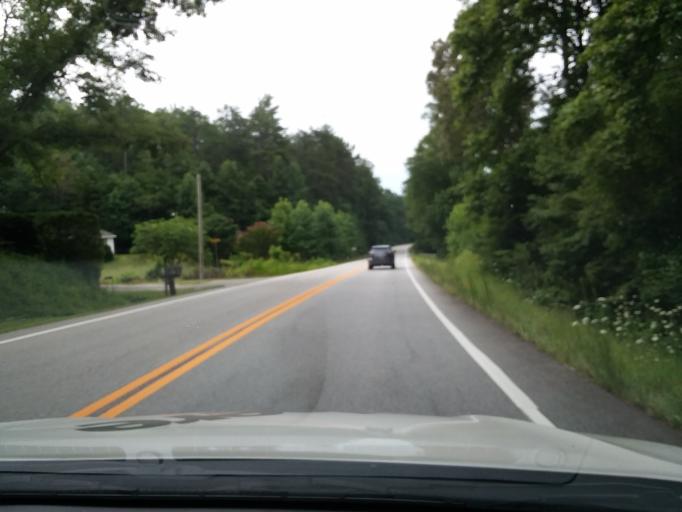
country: US
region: Georgia
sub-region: Rabun County
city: Clayton
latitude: 34.8200
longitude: -83.3192
